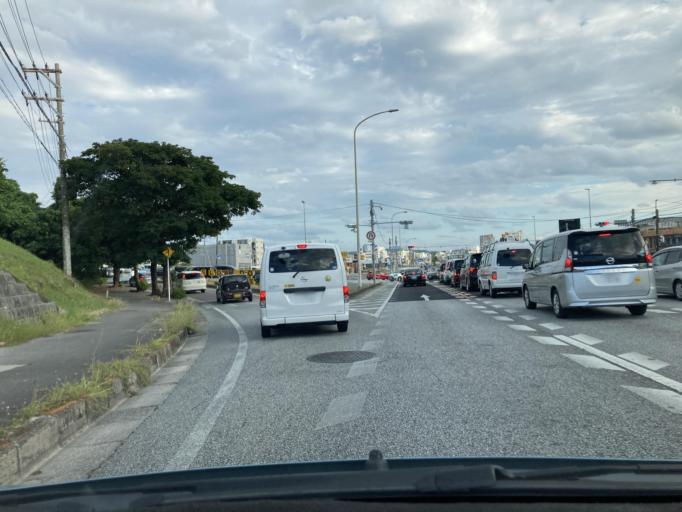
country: JP
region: Okinawa
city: Chatan
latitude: 26.3276
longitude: 127.7532
